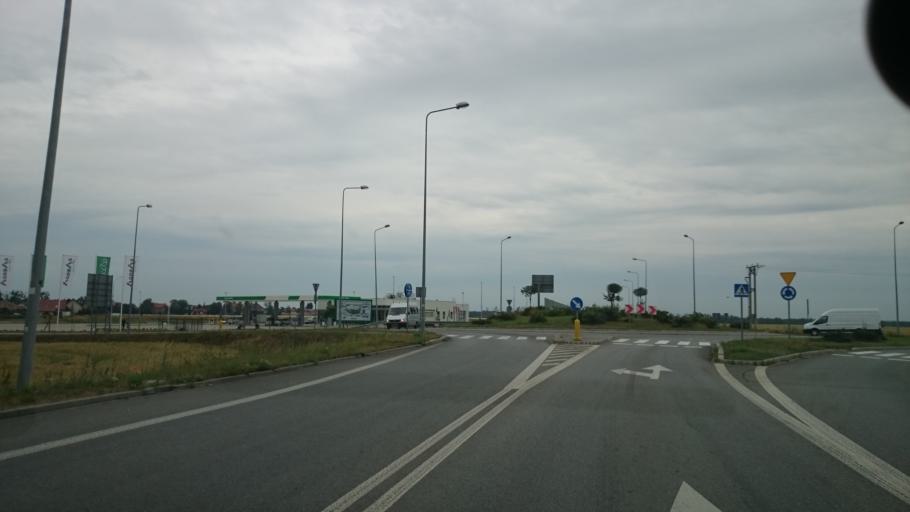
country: PL
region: Opole Voivodeship
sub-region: Powiat brzeski
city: Grodkow
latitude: 50.6835
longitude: 17.3856
